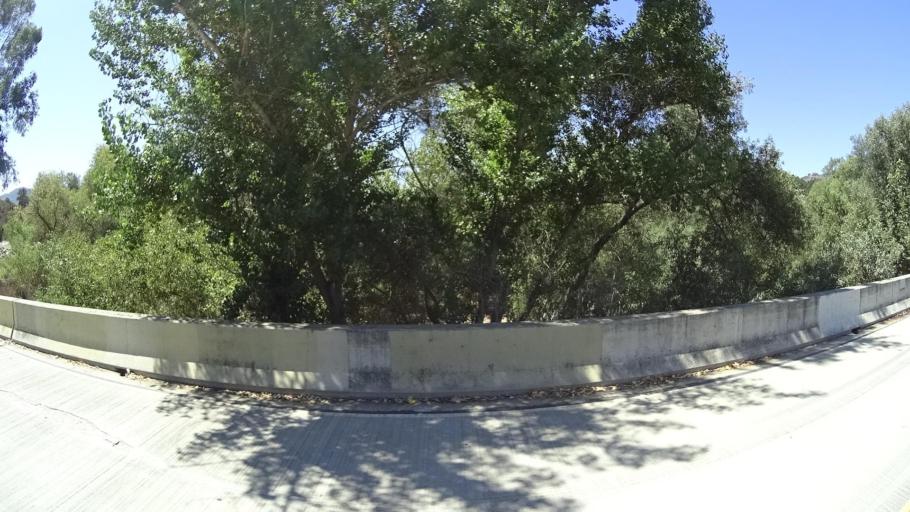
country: US
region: California
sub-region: San Diego County
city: Rainbow
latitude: 33.3326
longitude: -117.1494
